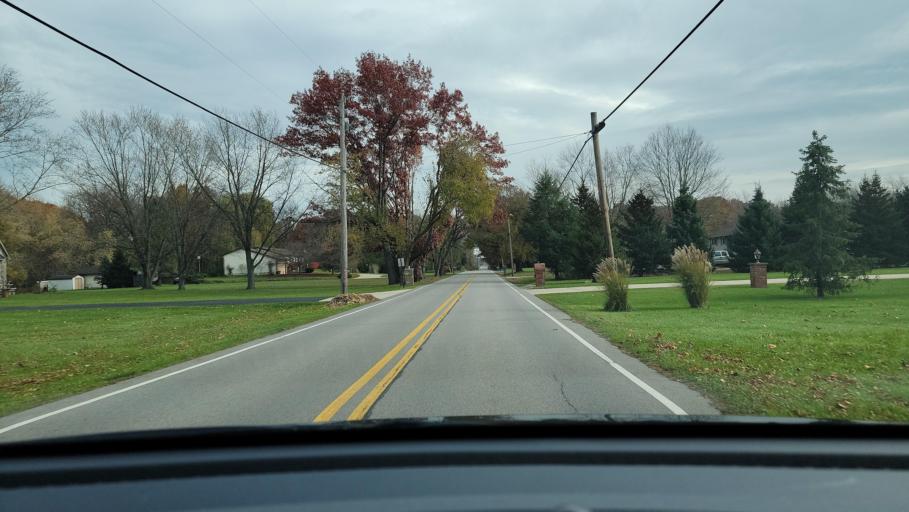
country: US
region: Indiana
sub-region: Porter County
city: Burns Harbor
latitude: 41.5865
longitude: -87.1340
